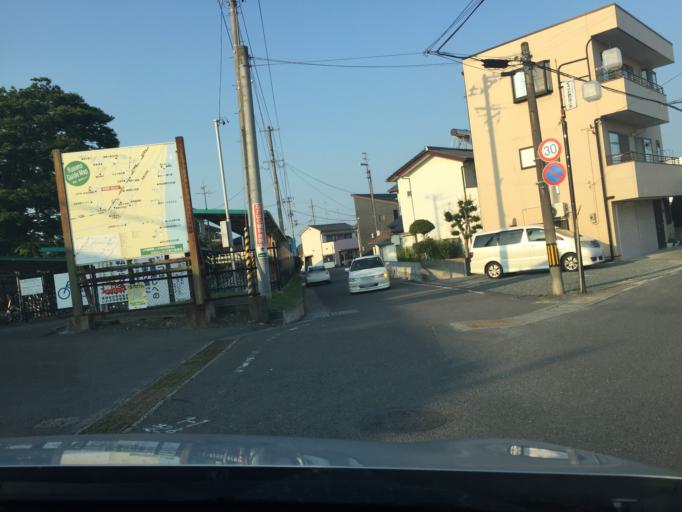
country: JP
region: Fukushima
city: Iwaki
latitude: 37.0737
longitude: 140.9477
